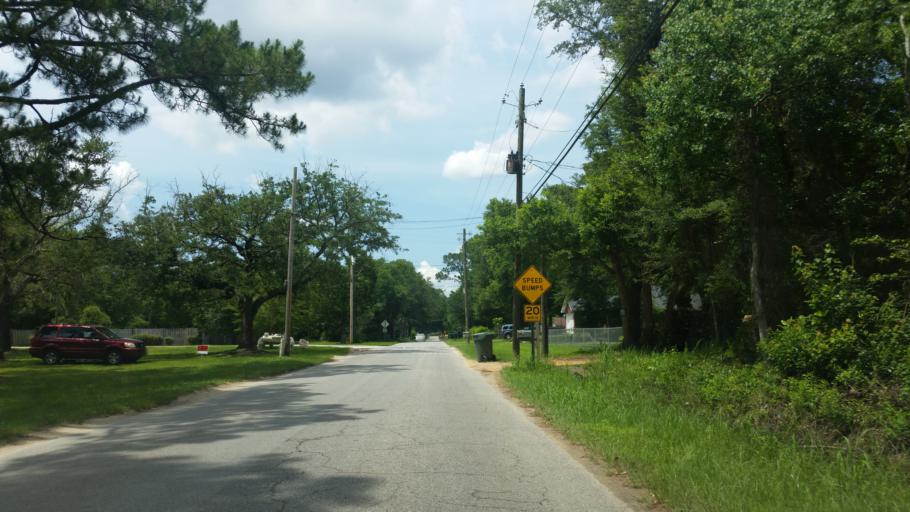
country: US
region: Florida
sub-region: Escambia County
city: Ensley
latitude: 30.5113
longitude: -87.2545
